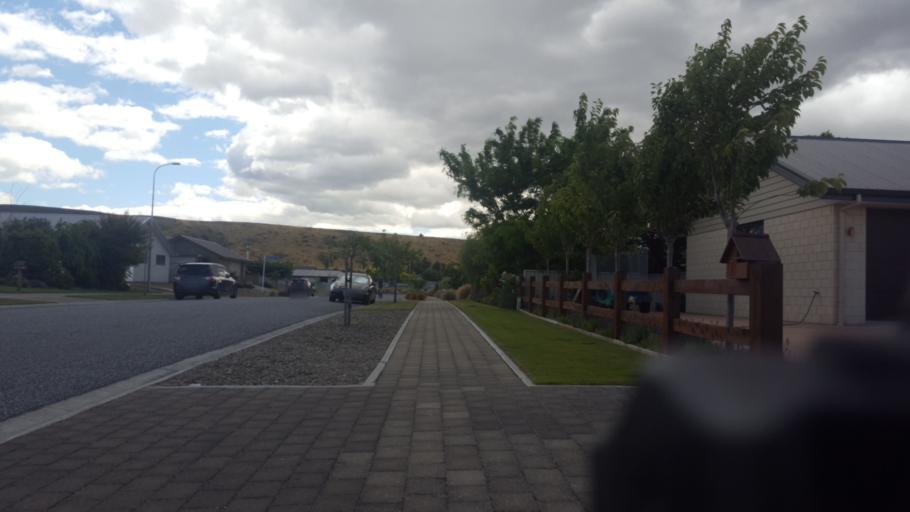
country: NZ
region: Otago
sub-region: Queenstown-Lakes District
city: Wanaka
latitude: -45.1968
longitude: 169.3319
